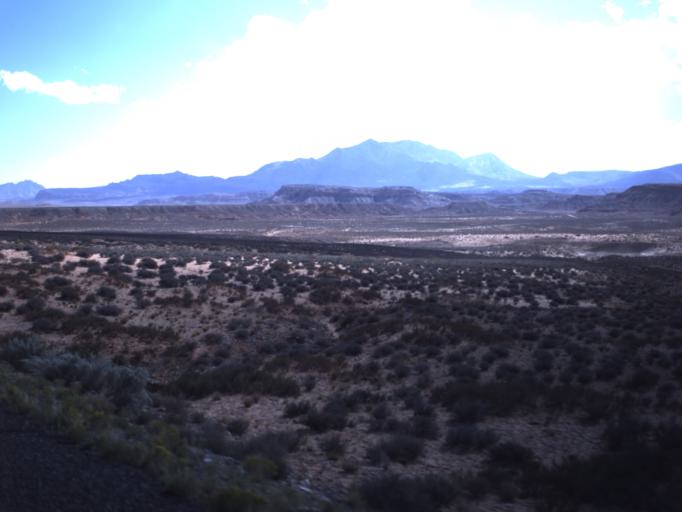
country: US
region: Utah
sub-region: Wayne County
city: Loa
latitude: 38.0840
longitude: -110.6142
